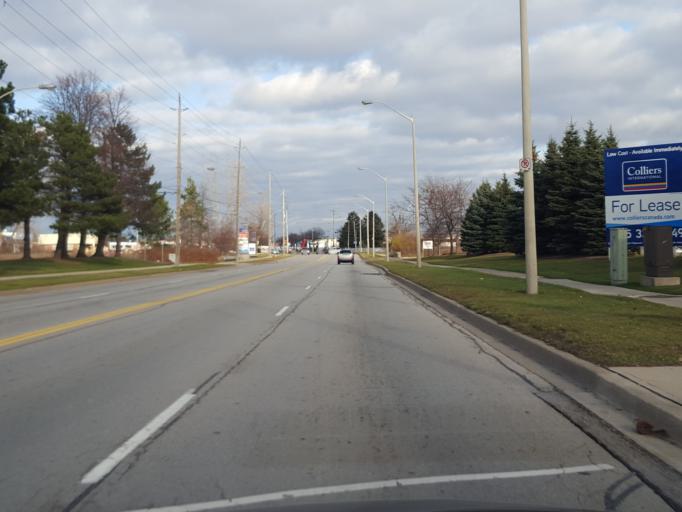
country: CA
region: Ontario
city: Burlington
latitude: 43.3606
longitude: -79.7872
